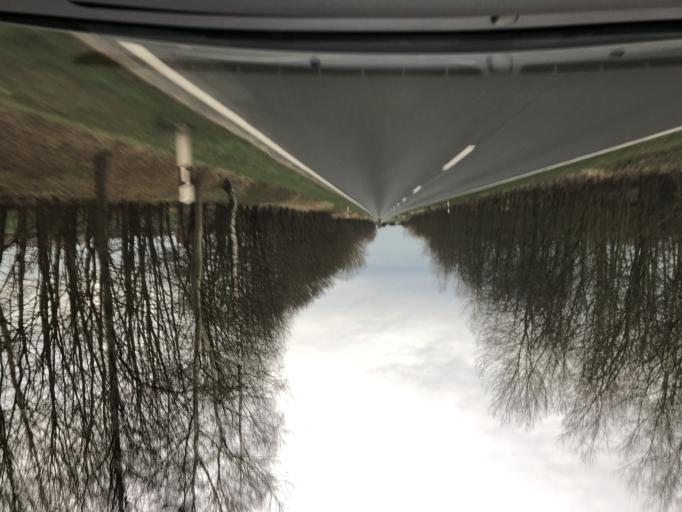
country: DE
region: Mecklenburg-Vorpommern
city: Ostseebad Dierhagen
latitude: 54.2314
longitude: 12.3649
